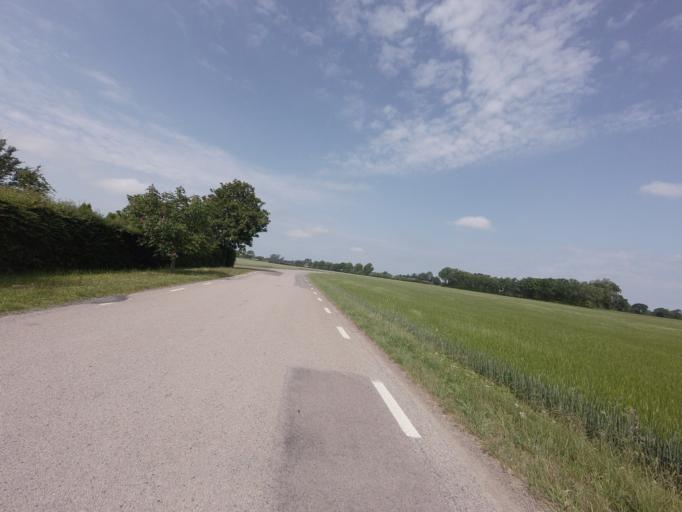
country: SE
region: Skane
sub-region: Hoganas Kommun
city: Hoganas
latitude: 56.1838
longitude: 12.6605
